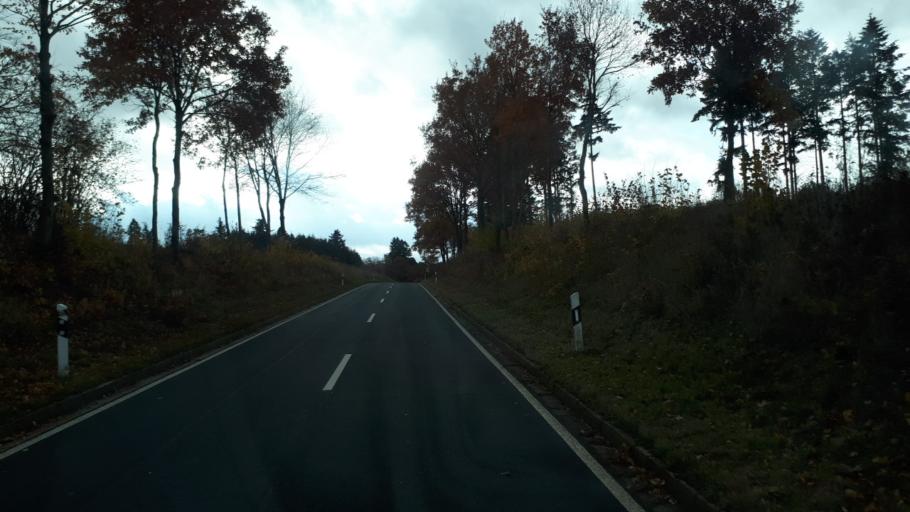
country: DE
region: Rheinland-Pfalz
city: Wirfus
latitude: 50.2134
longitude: 7.2021
